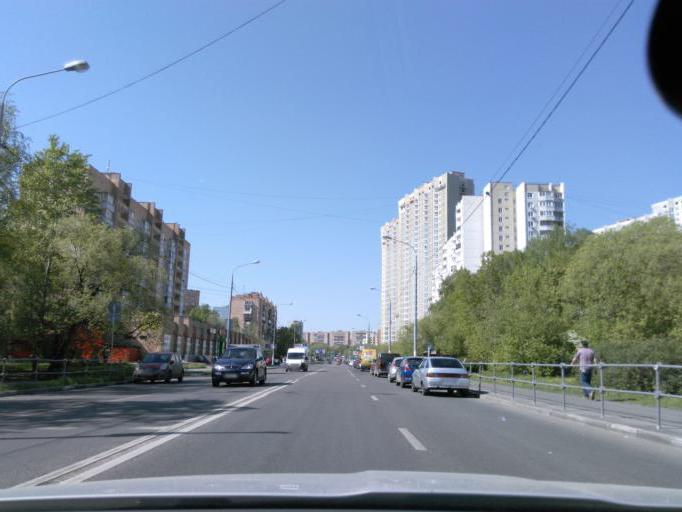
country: RU
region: Moscow
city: Golovinskiy
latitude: 55.8549
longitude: 37.5031
